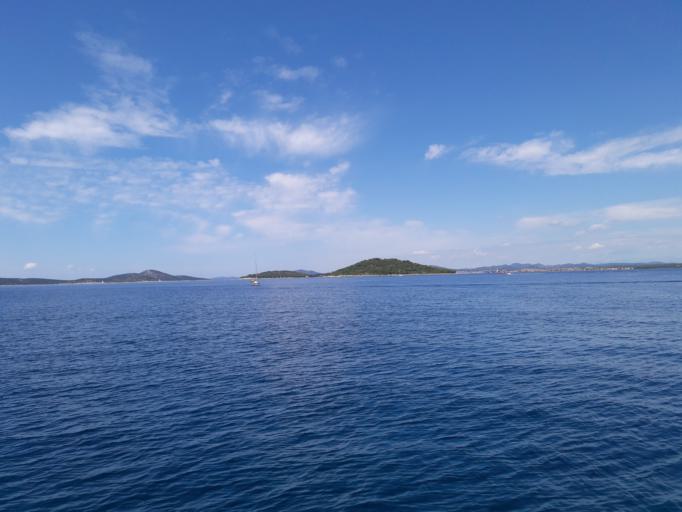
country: HR
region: Sibensko-Kniniska
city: Vodice
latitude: 43.7031
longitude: 15.8298
